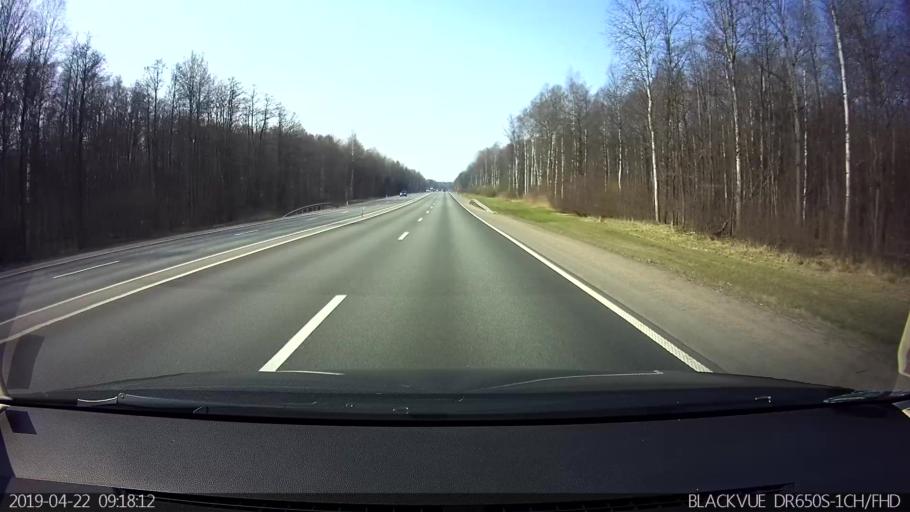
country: RU
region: Smolensk
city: Golynki
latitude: 54.7559
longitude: 31.4973
